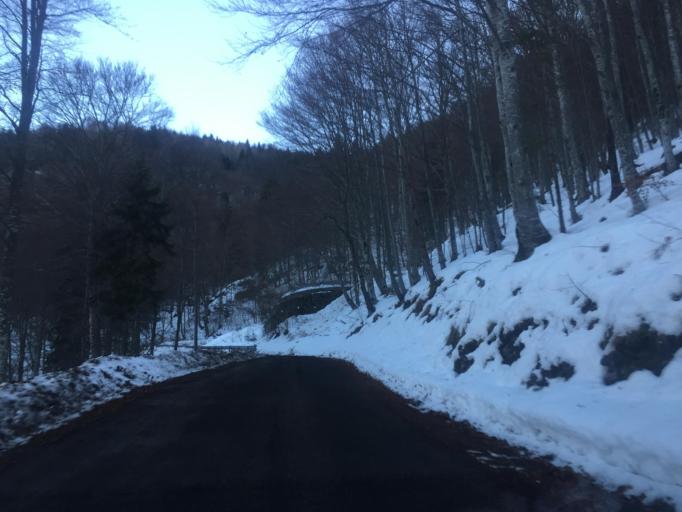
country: IT
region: Friuli Venezia Giulia
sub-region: Provincia di Udine
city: Lauco
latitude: 46.4515
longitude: 12.9286
